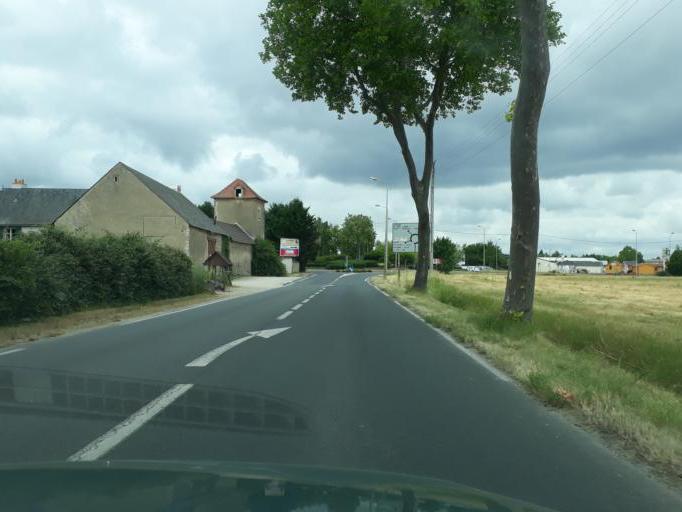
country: FR
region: Centre
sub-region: Departement du Loiret
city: Saint-Denis-en-Val
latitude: 47.8734
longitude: 1.9468
